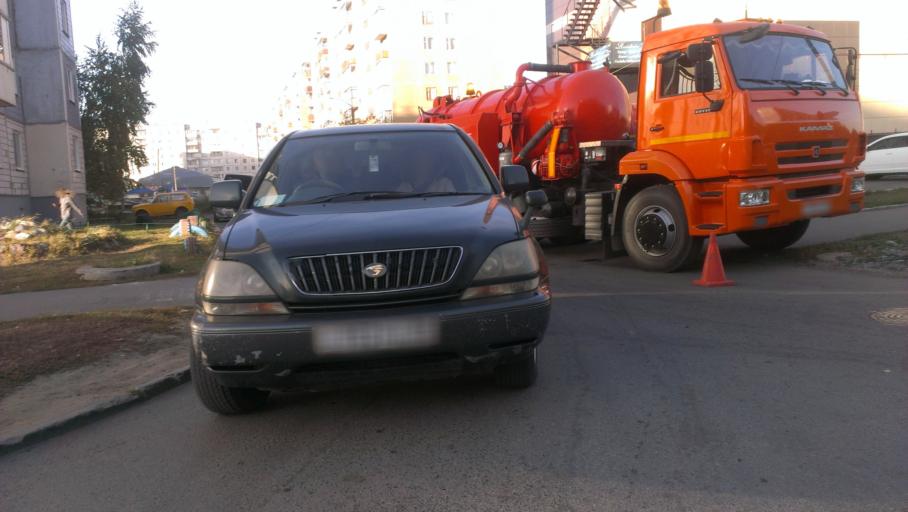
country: RU
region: Altai Krai
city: Novosilikatnyy
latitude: 53.3394
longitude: 83.6717
